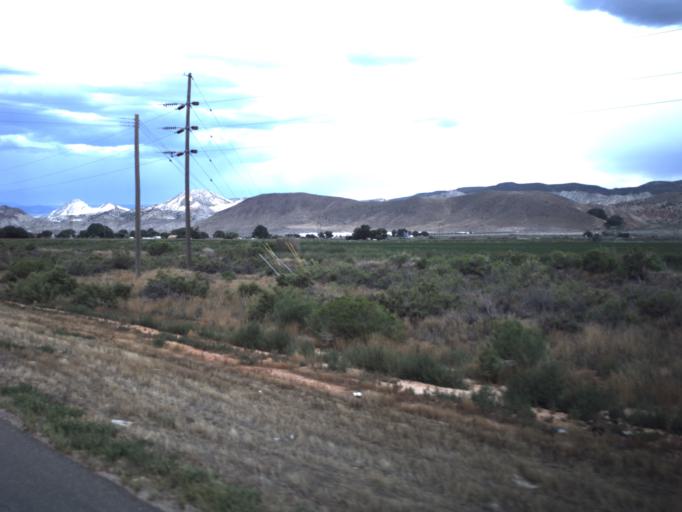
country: US
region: Utah
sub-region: Sevier County
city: Richfield
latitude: 38.8291
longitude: -111.9918
